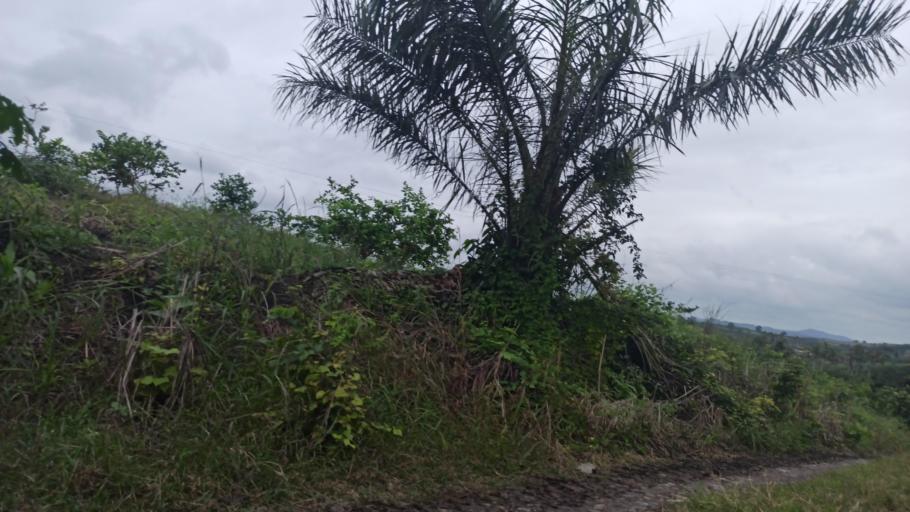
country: MX
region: Puebla
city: Espinal
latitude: 20.3011
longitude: -97.4091
